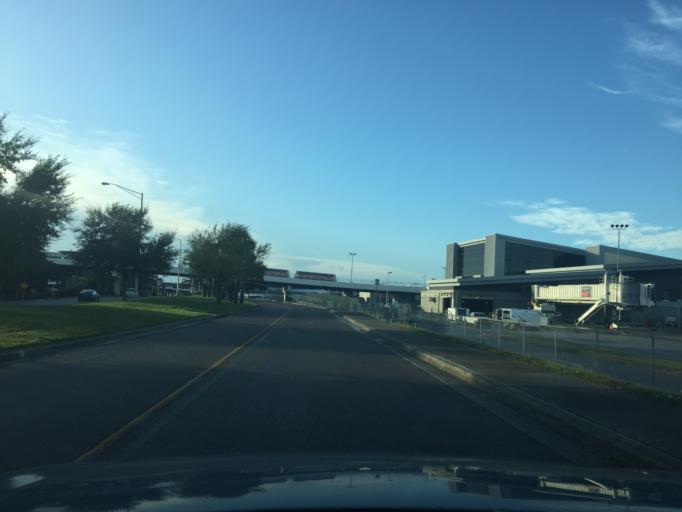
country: US
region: Florida
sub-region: Hillsborough County
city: Egypt Lake-Leto
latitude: 27.9815
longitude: -82.5369
